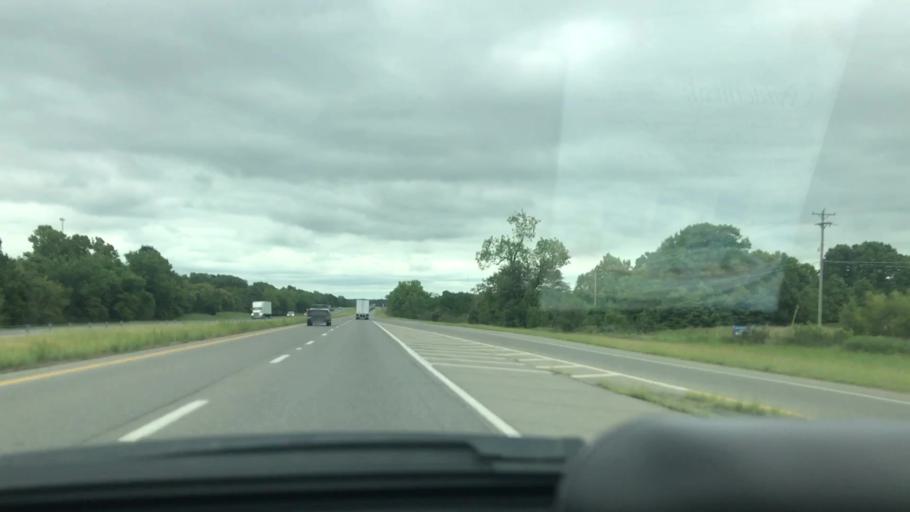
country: US
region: Oklahoma
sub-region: McIntosh County
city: Eufaula
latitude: 35.3645
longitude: -95.5730
